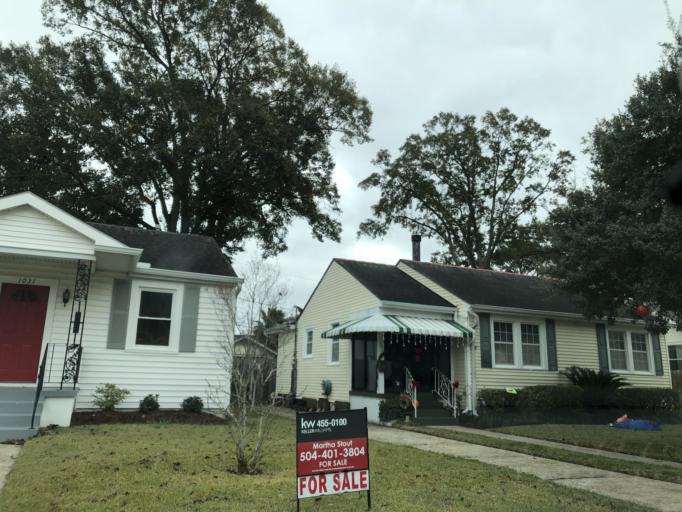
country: US
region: Louisiana
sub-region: Jefferson Parish
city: Metairie Terrace
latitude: 29.9736
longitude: -90.1680
